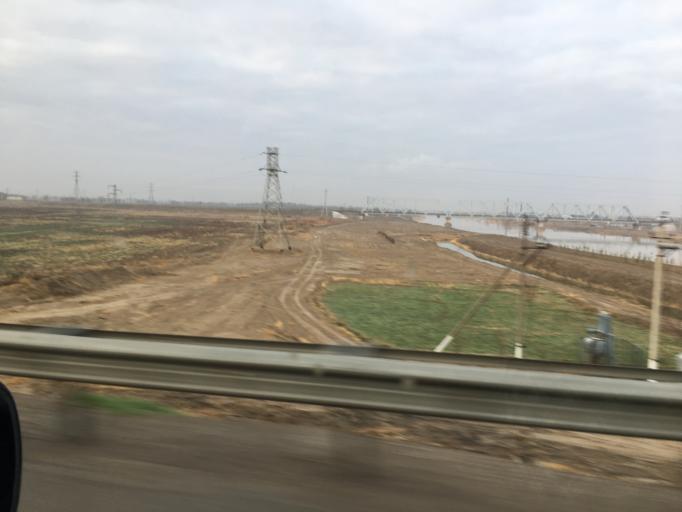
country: TM
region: Mary
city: Mary
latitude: 37.5479
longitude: 61.8669
